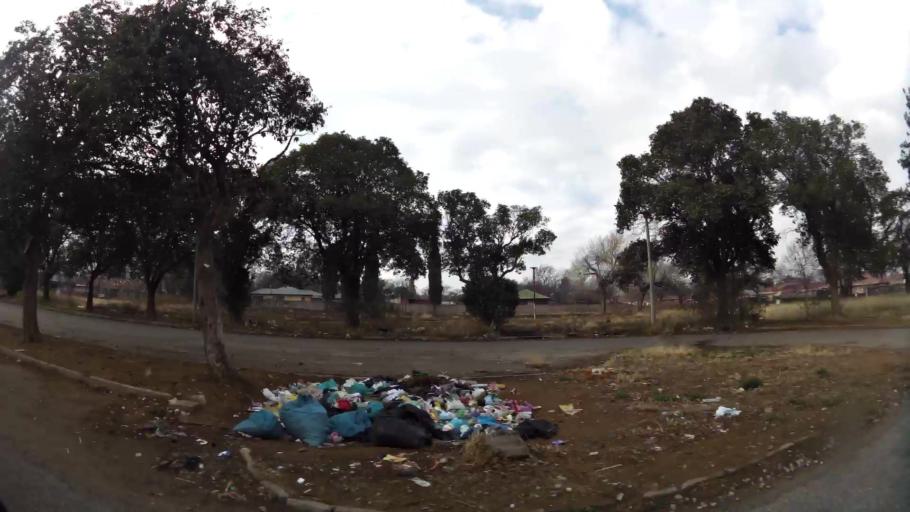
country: ZA
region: Gauteng
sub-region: Sedibeng District Municipality
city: Vanderbijlpark
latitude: -26.6922
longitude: 27.8197
